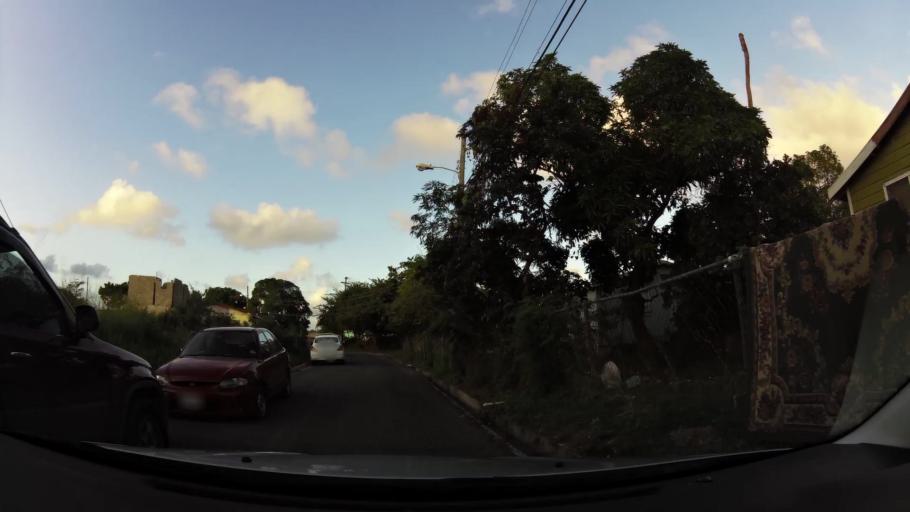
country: AG
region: Saint John
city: Saint John's
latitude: 17.1307
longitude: -61.8383
